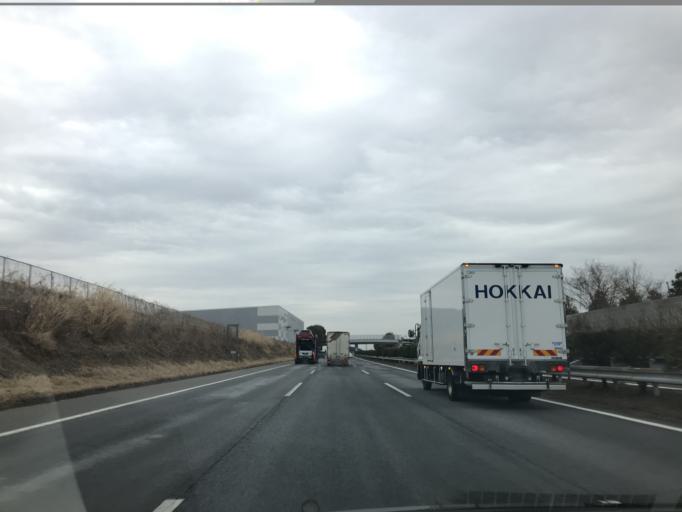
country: JP
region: Ibaraki
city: Mitsukaido
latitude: 36.0027
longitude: 140.0393
